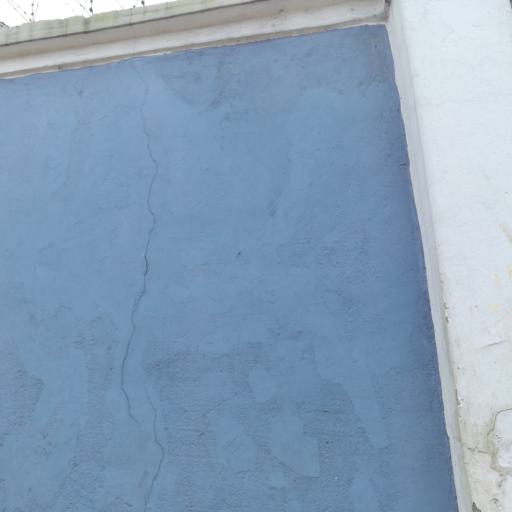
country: NG
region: Rivers
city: Port Harcourt
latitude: 4.8343
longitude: 7.0764
